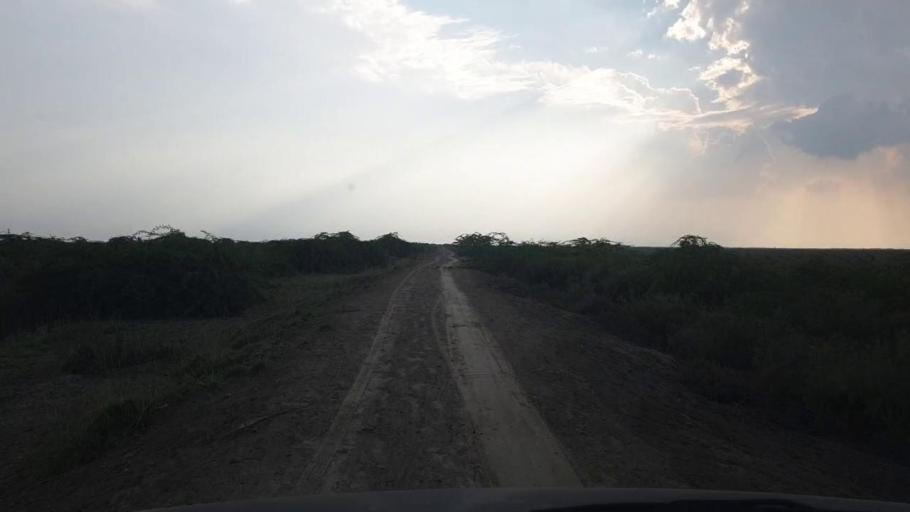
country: PK
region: Sindh
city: Badin
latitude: 24.4649
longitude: 68.6927
